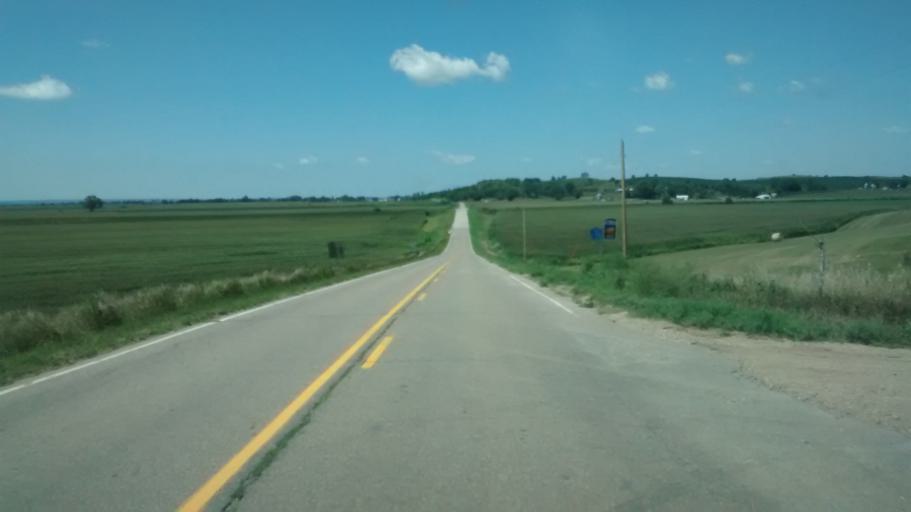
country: US
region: Iowa
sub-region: Woodbury County
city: Moville
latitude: 42.2615
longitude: -96.0452
